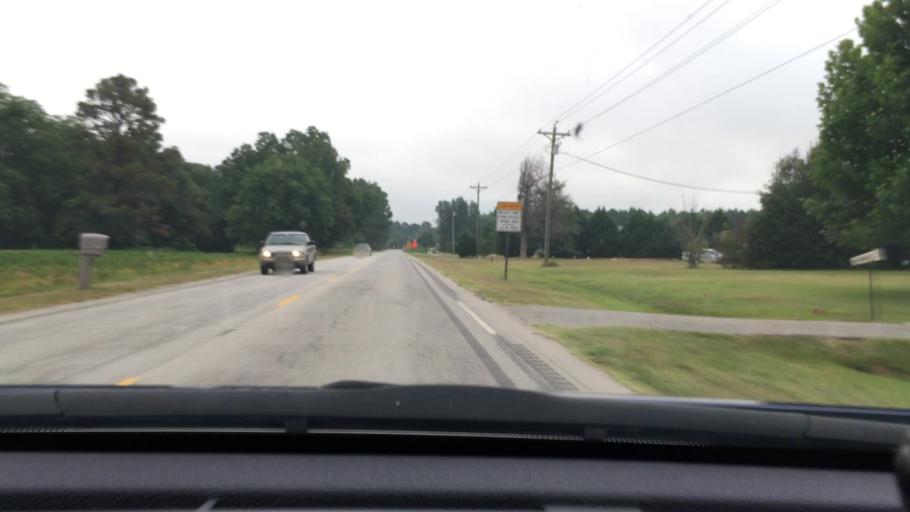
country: US
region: South Carolina
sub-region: Florence County
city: Timmonsville
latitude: 34.2297
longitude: -79.9873
